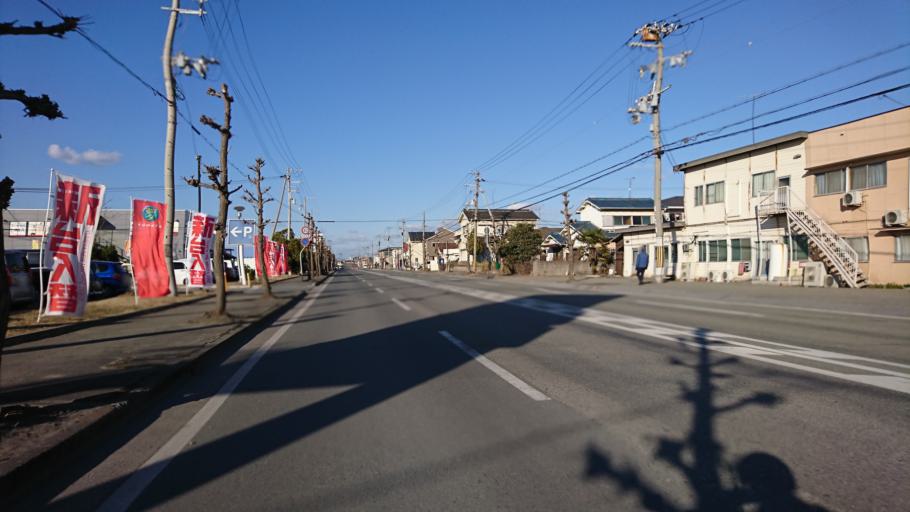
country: JP
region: Hyogo
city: Kakogawacho-honmachi
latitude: 34.7329
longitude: 134.8215
